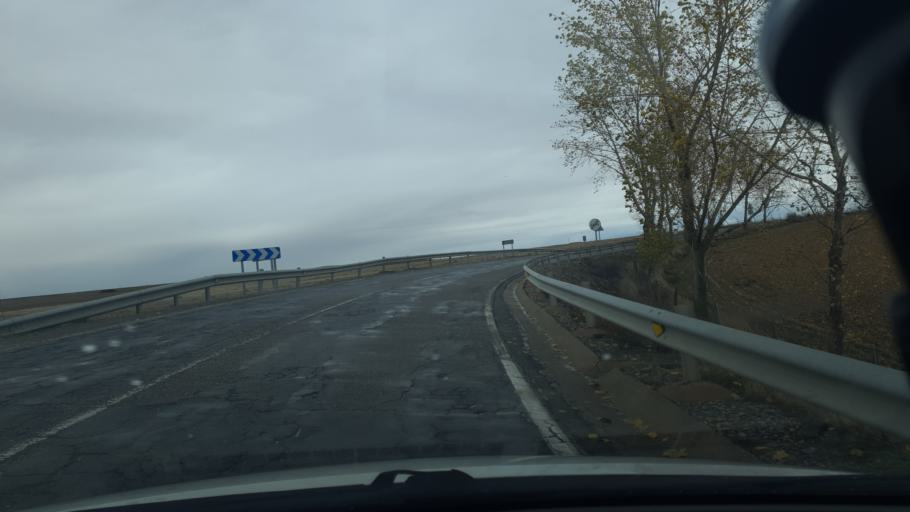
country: ES
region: Castille and Leon
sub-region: Provincia de Segovia
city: Segovia
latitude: 40.9673
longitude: -4.1409
